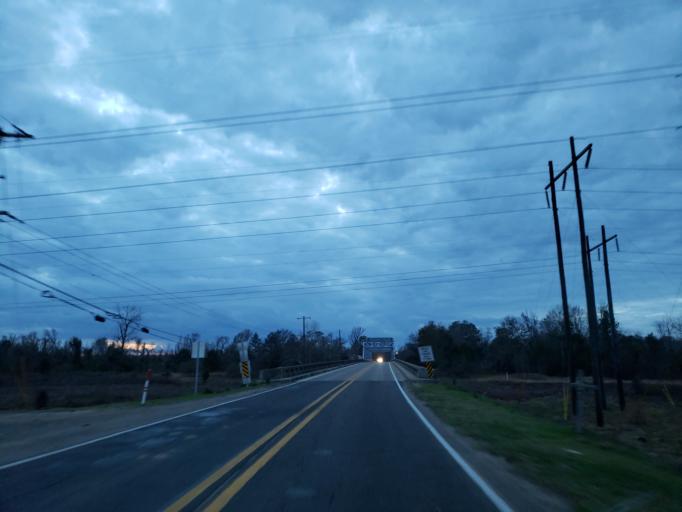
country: US
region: Mississippi
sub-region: Forrest County
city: Petal
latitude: 31.3277
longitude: -89.2652
